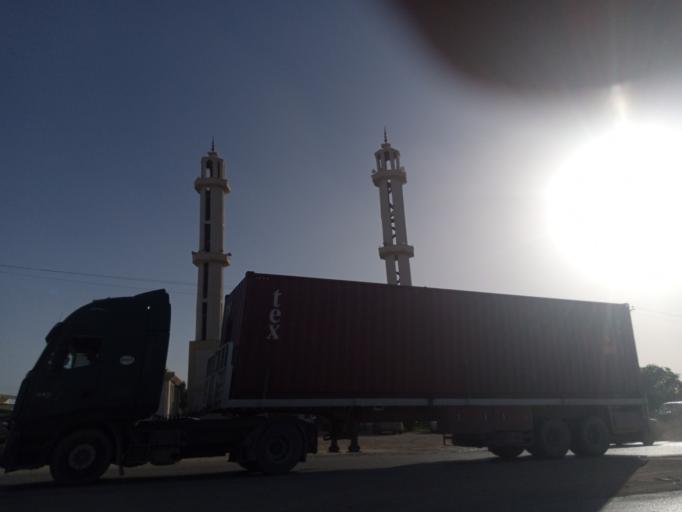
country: LY
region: Al Marqab
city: Masallatah
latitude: 32.7040
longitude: 13.8922
